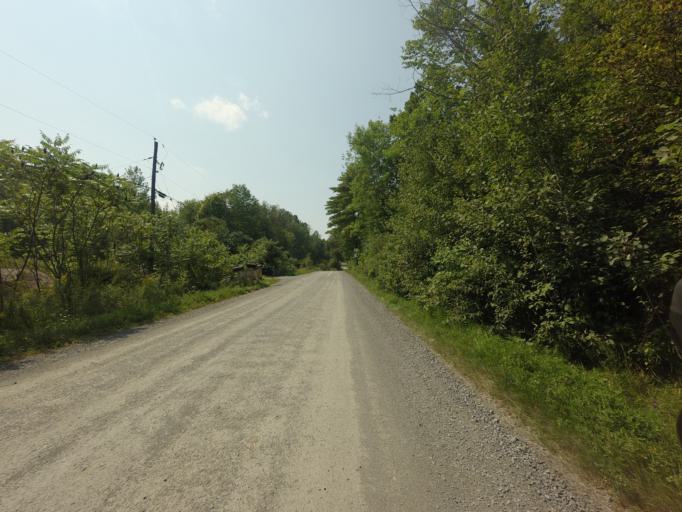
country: CA
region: Ontario
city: Kingston
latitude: 44.6411
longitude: -76.6281
